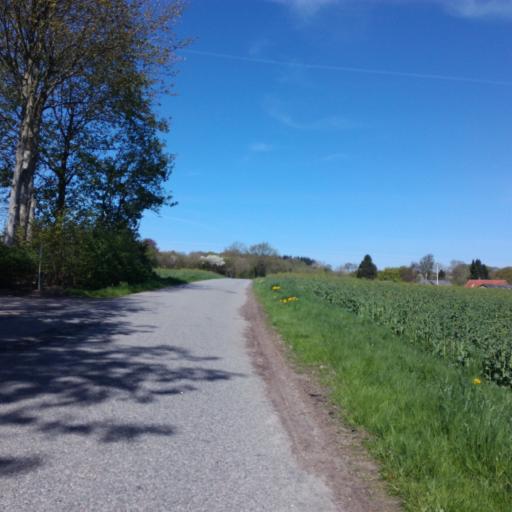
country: DK
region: South Denmark
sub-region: Vejle Kommune
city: Borkop
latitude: 55.6221
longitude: 9.6567
